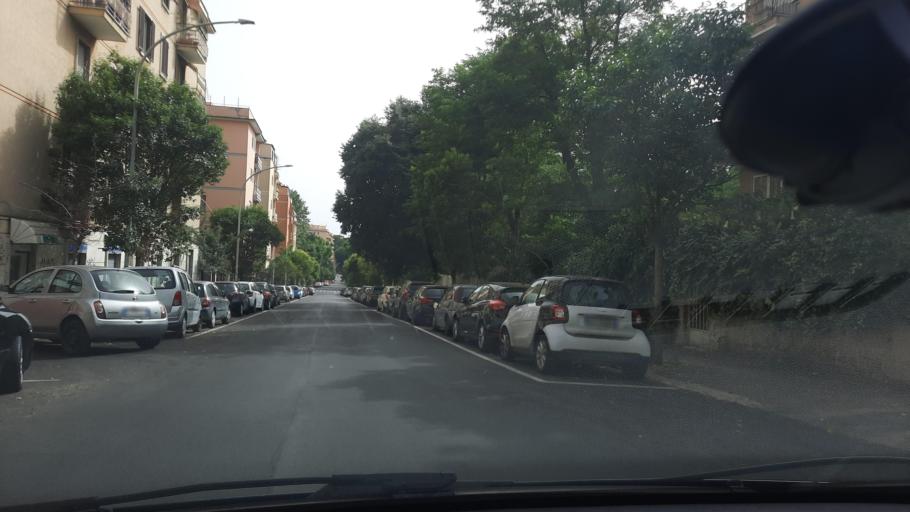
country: IT
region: Latium
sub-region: Citta metropolitana di Roma Capitale
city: Rome
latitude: 41.8581
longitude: 12.4893
